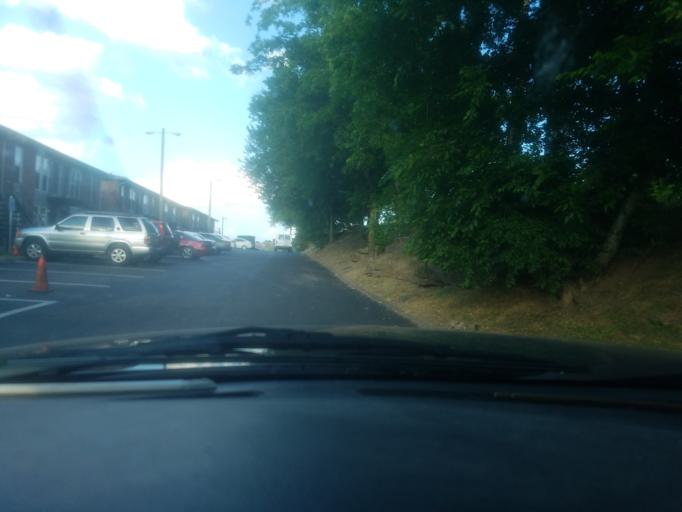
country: US
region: Tennessee
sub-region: Davidson County
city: Nashville
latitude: 36.1611
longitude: -86.8429
